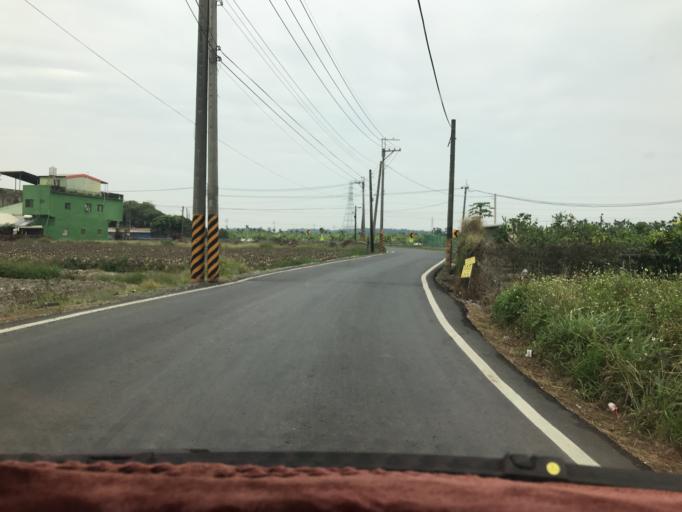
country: TW
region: Taiwan
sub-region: Pingtung
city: Pingtung
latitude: 22.5335
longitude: 120.5596
